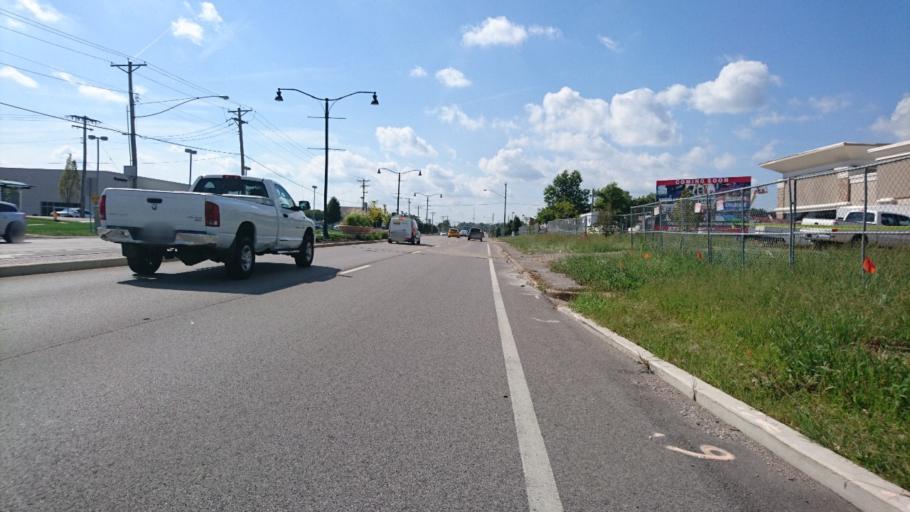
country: US
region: Missouri
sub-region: Saint Louis County
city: Ellisville
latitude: 38.5928
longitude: -90.5776
